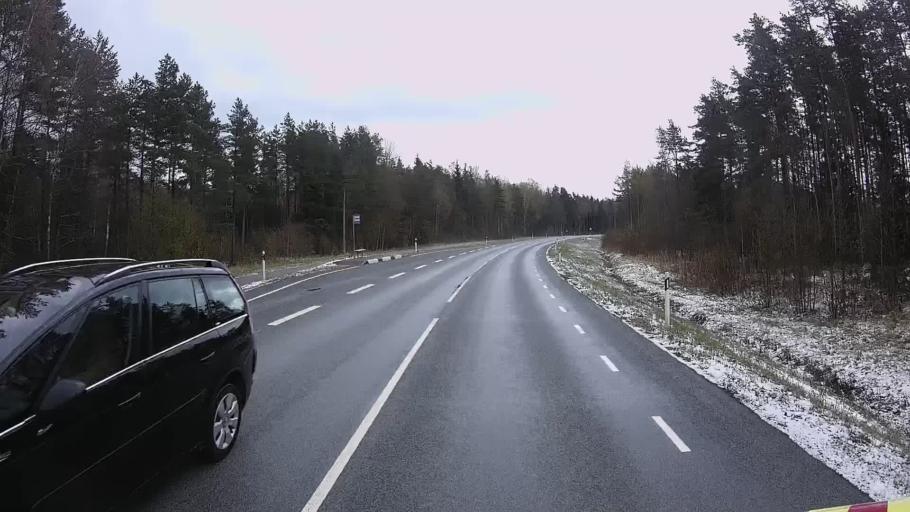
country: EE
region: Hiiumaa
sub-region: Kaerdla linn
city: Kardla
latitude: 59.0104
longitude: 22.6760
